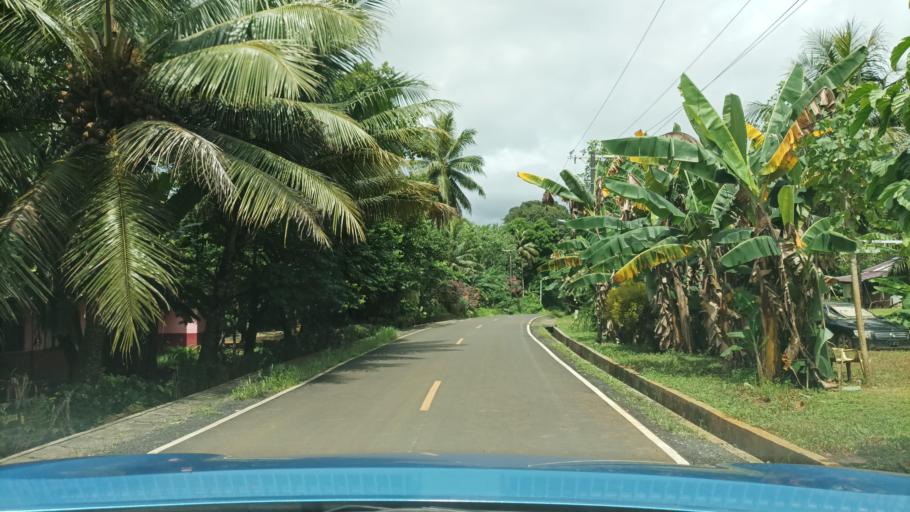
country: FM
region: Pohnpei
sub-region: Madolenihm Municipality
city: Madolenihm Municipality Government
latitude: 6.8822
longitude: 158.3226
